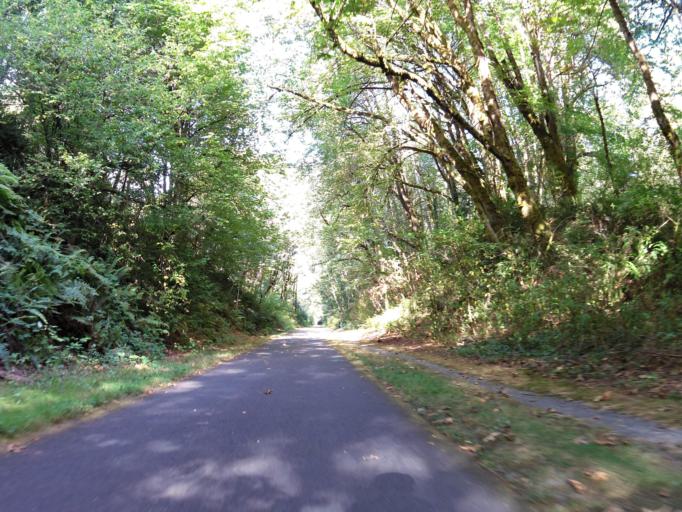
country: US
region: Washington
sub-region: Thurston County
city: Olympia
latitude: 47.0332
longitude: -122.8804
